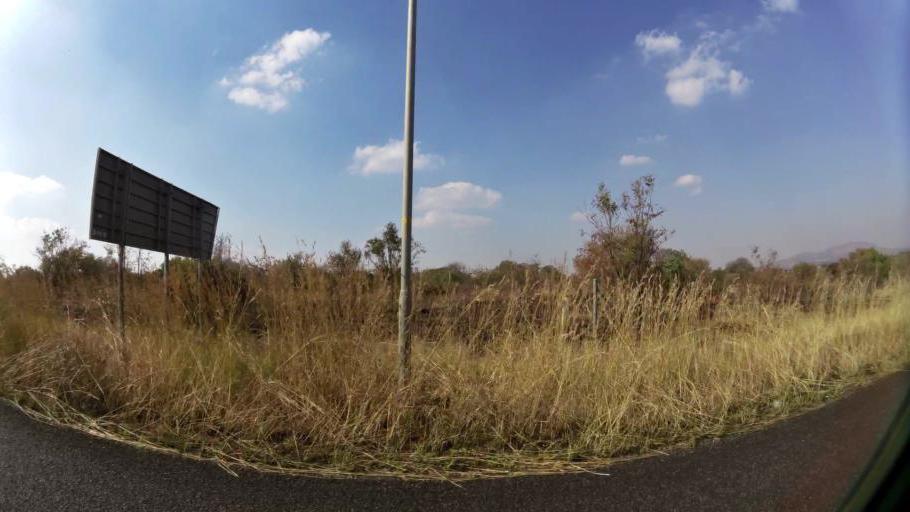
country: ZA
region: North-West
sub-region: Bojanala Platinum District Municipality
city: Rustenburg
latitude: -25.5929
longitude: 27.1278
